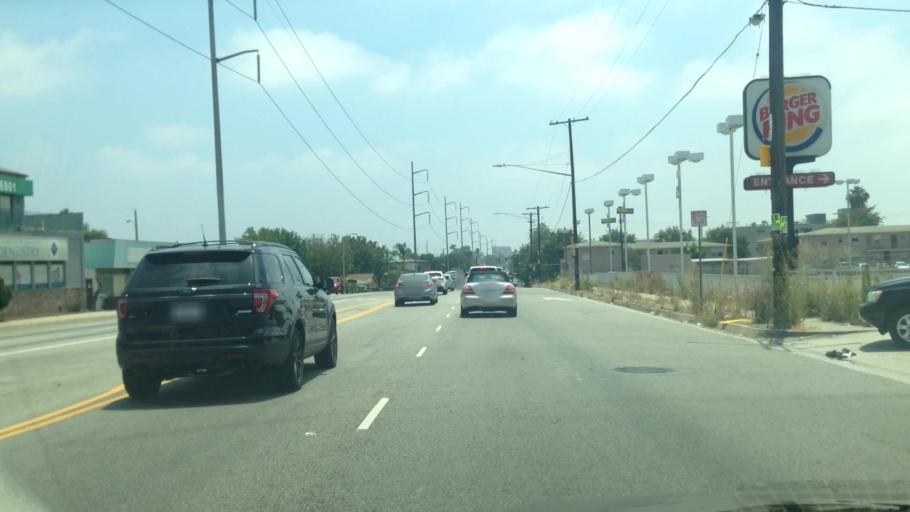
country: US
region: California
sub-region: Los Angeles County
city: Ladera Heights
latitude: 33.9768
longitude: -118.3704
